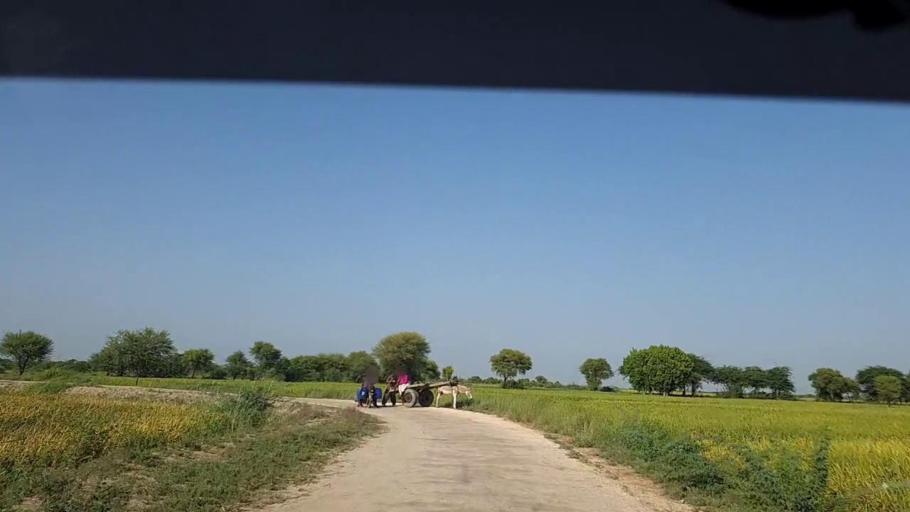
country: PK
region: Sindh
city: Badin
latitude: 24.6847
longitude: 68.8414
